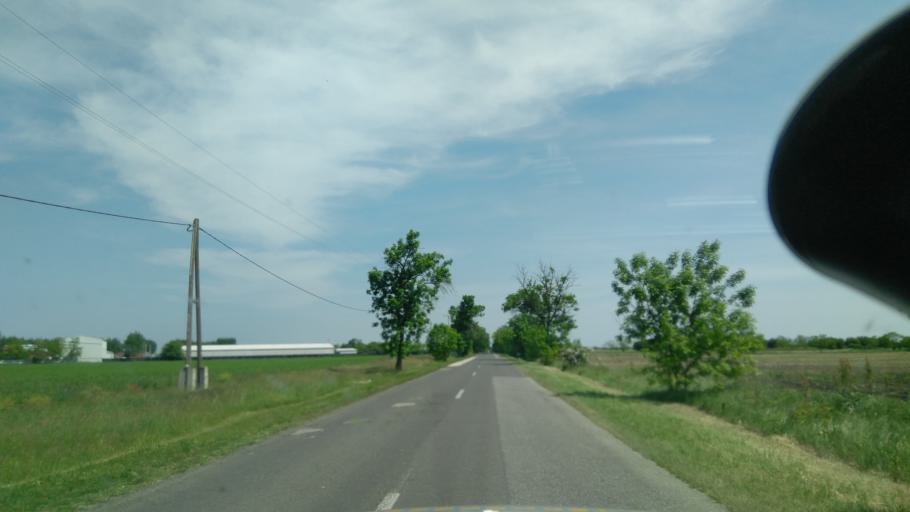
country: HU
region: Csongrad
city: Szekkutas
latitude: 46.5706
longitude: 20.5595
